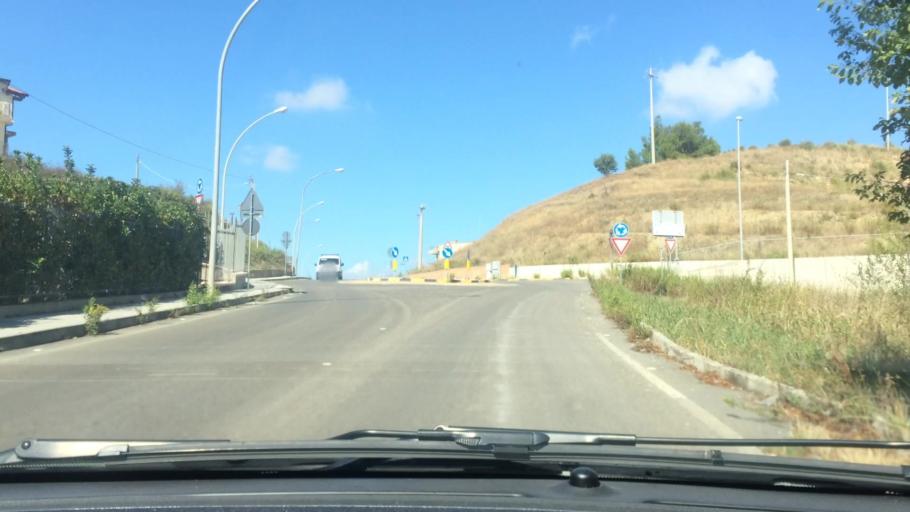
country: IT
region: Basilicate
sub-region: Provincia di Matera
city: Montescaglioso
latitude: 40.5443
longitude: 16.6691
